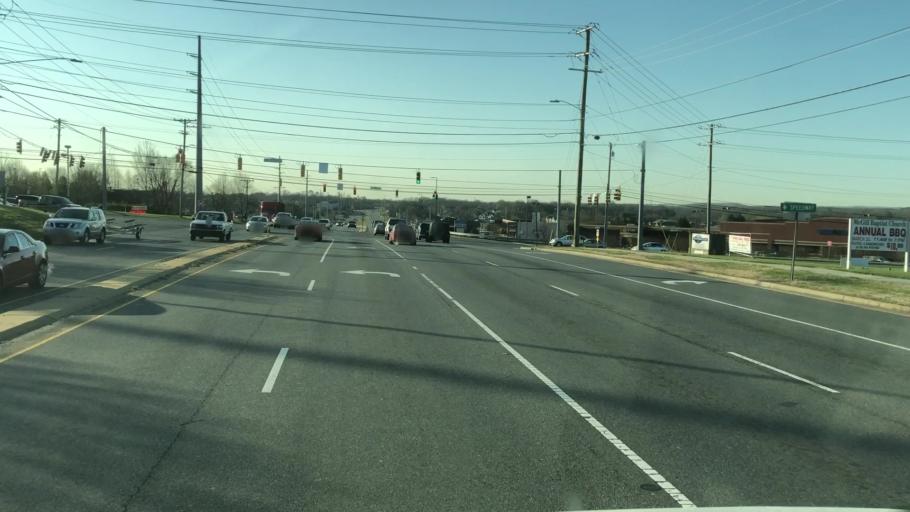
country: US
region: North Carolina
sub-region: Cabarrus County
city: Concord
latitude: 35.4132
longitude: -80.6666
